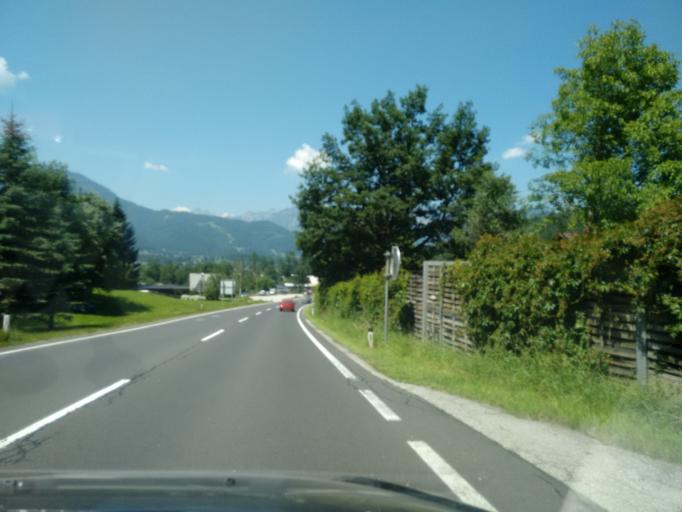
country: AT
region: Upper Austria
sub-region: Politischer Bezirk Gmunden
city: Bad Goisern
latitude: 47.6209
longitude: 13.6494
